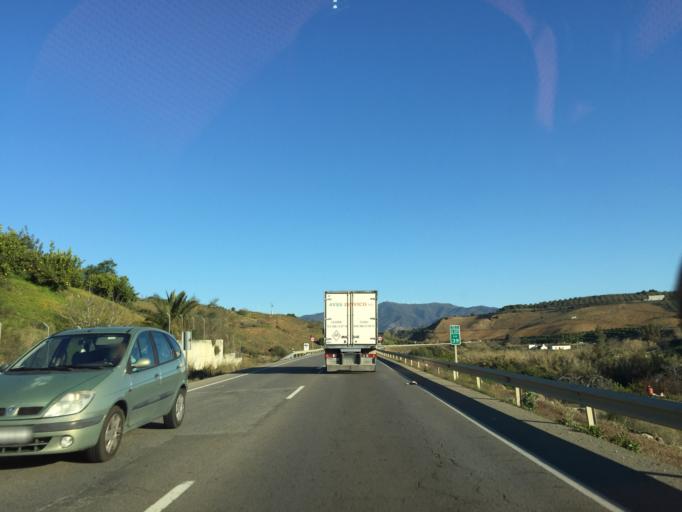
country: ES
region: Andalusia
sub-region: Provincia de Malaga
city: Pizarra
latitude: 36.7736
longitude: -4.7399
